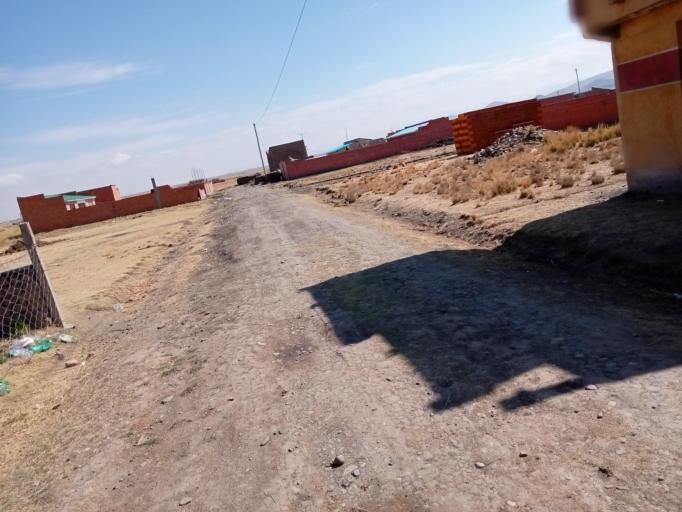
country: BO
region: La Paz
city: Batallas
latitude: -16.4379
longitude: -68.3747
